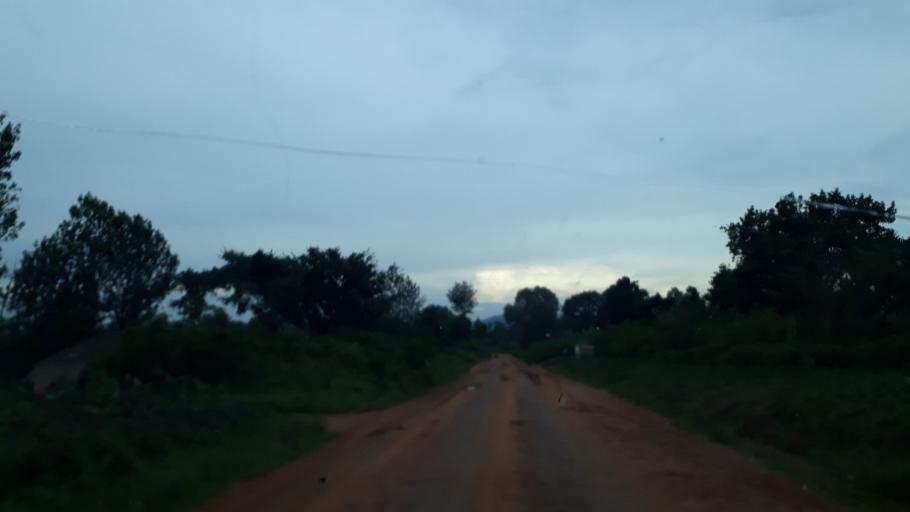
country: UG
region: Northern Region
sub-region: Zombo District
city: Paidha
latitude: 2.2182
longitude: 30.7761
